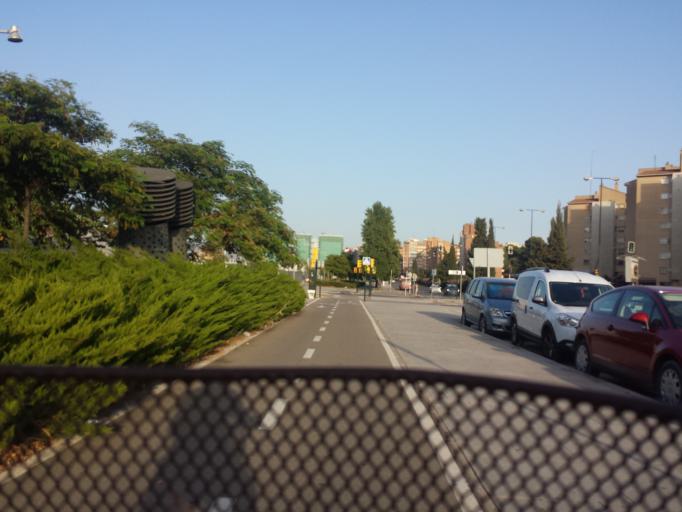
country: ES
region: Aragon
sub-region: Provincia de Zaragoza
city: Delicias
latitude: 41.6577
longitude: -0.9148
